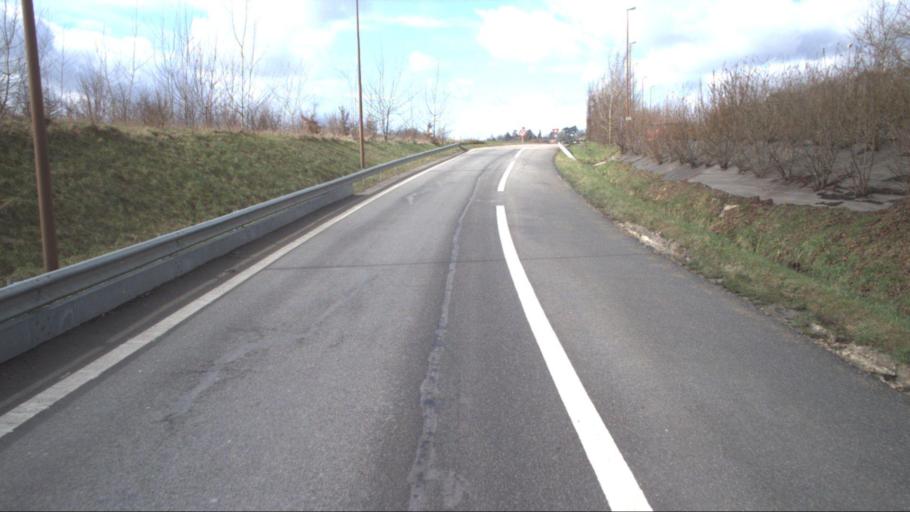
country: FR
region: Ile-de-France
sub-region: Departement des Yvelines
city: Mere
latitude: 48.8013
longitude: 1.8158
